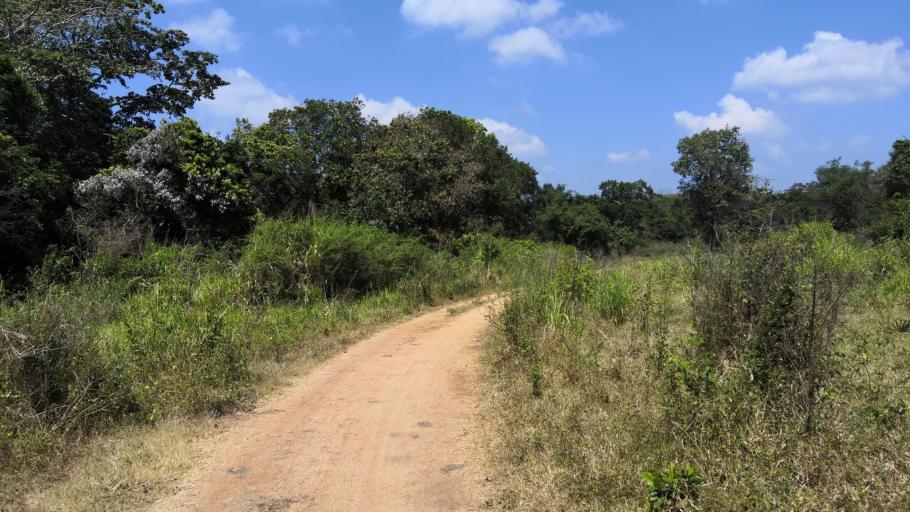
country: LK
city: Padaviya Divisional Secretariat
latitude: 8.9574
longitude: 80.6979
